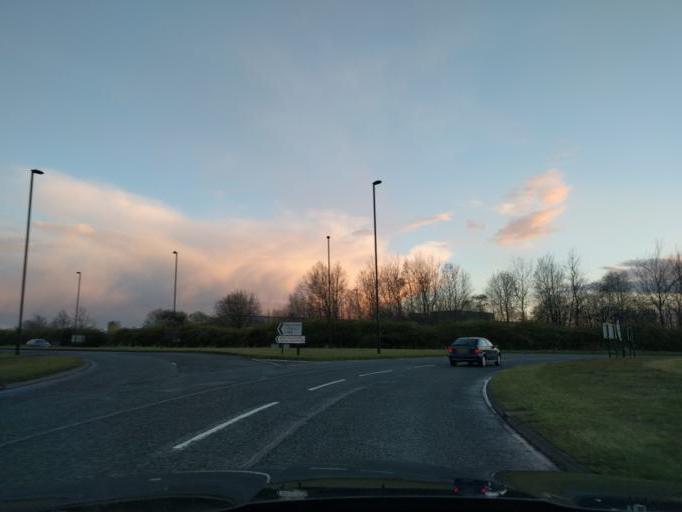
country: GB
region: England
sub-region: Newcastle upon Tyne
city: Gosforth
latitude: 55.0252
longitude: -1.5859
